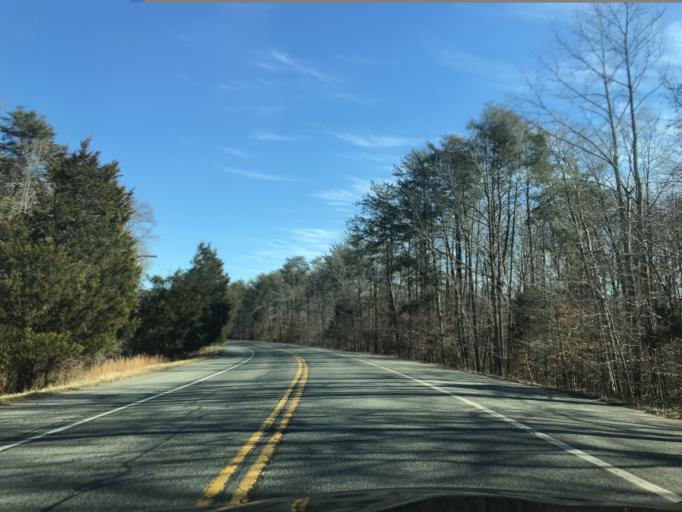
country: US
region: Virginia
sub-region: Prince William County
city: Cherry Hill
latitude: 38.5312
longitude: -77.2123
